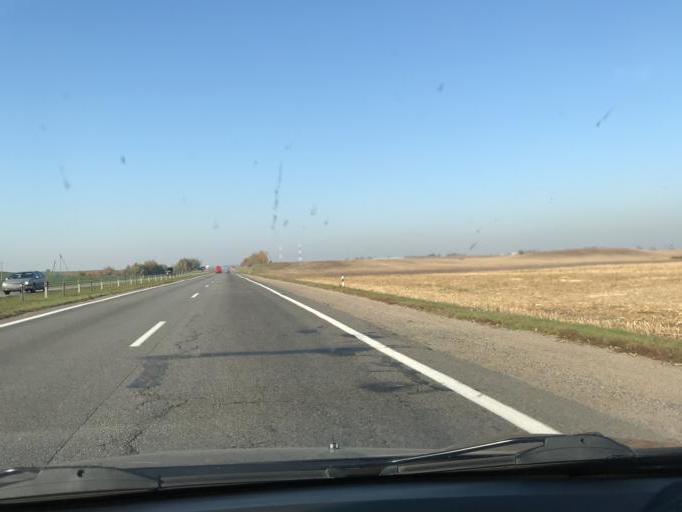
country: BY
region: Minsk
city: Luhavaya Slabada
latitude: 53.7245
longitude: 27.8592
